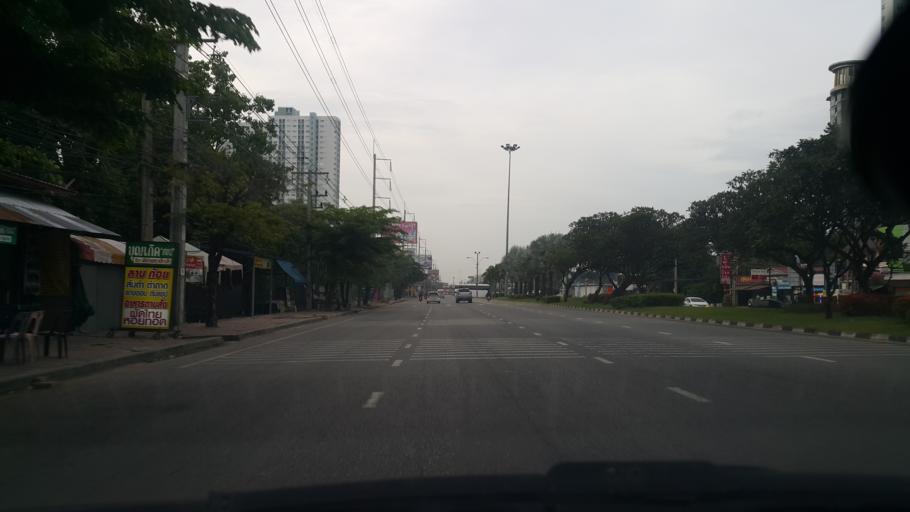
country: TH
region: Chon Buri
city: Phatthaya
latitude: 12.9608
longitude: 100.9087
